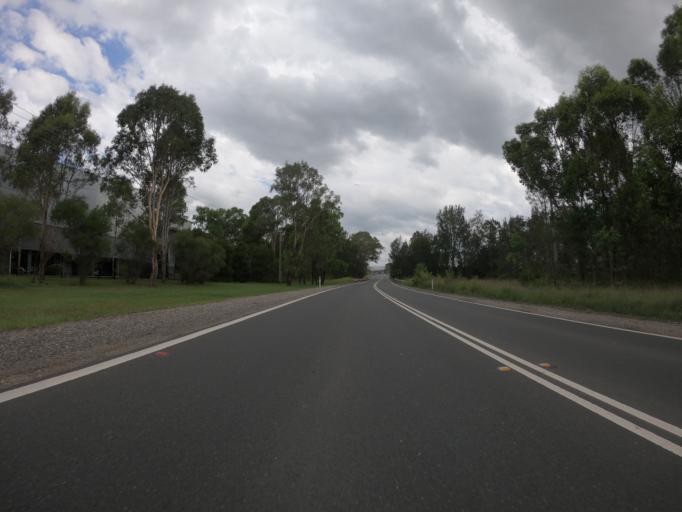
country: AU
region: New South Wales
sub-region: Blacktown
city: Mount Druitt
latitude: -33.8130
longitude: 150.7758
